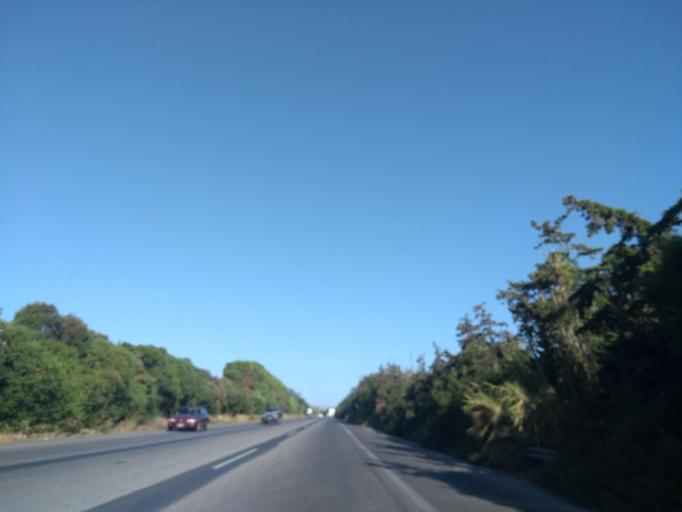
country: GR
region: Crete
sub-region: Nomos Chanias
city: Gerani
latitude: 35.5149
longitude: 23.8709
